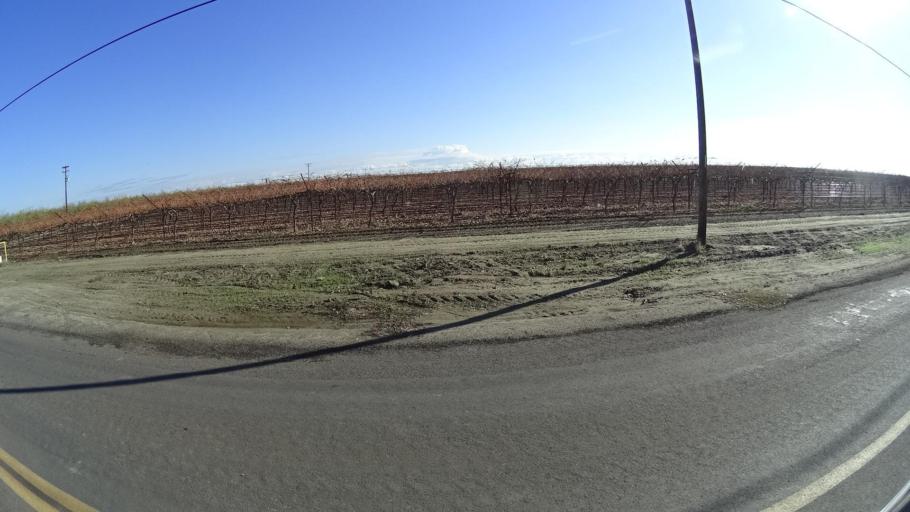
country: US
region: California
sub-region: Kern County
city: McFarland
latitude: 35.7029
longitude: -119.2764
